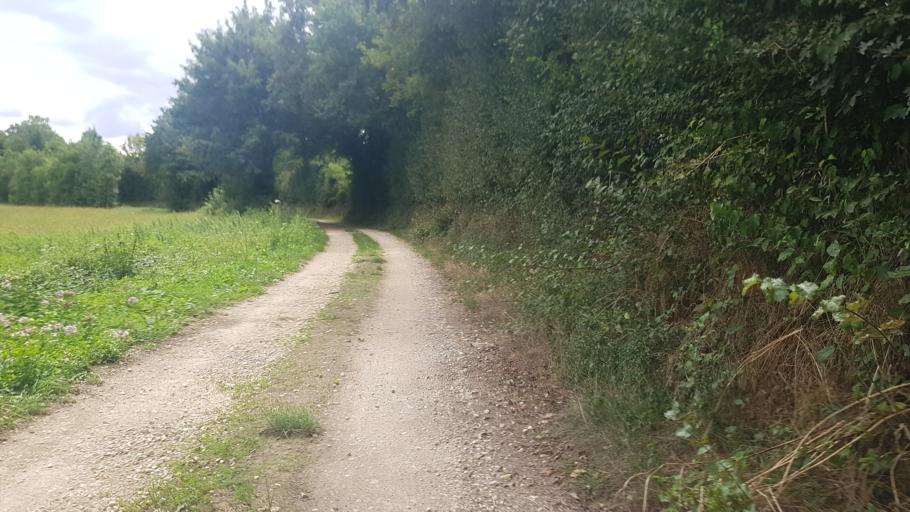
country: FR
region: Poitou-Charentes
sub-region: Departement des Deux-Sevres
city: Vouille
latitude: 46.3135
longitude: -0.3419
